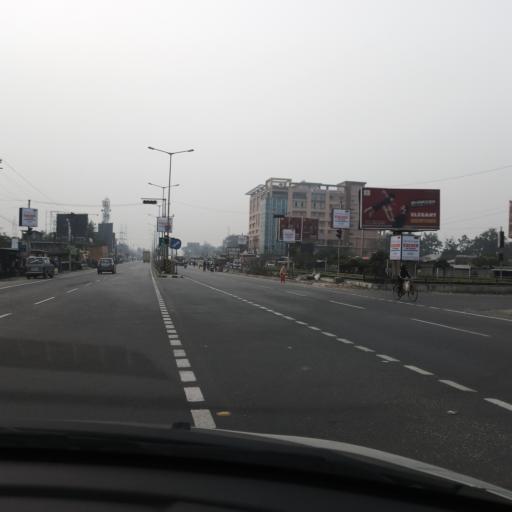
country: IN
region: West Bengal
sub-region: Darjiling
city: Shiliguri
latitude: 26.6571
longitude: 88.4166
